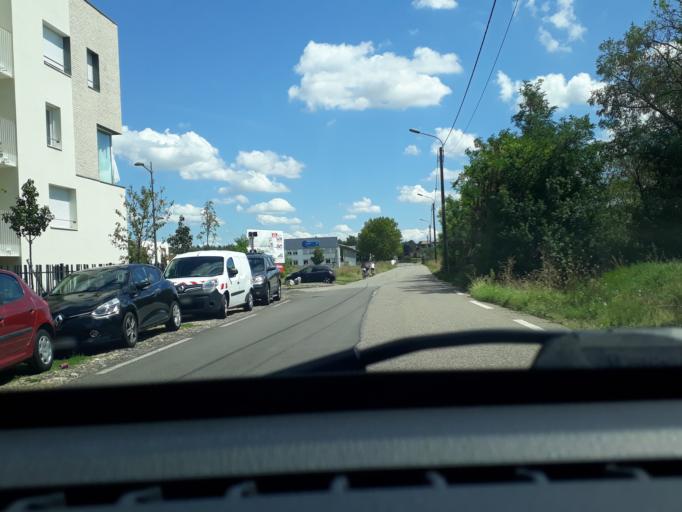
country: FR
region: Rhone-Alpes
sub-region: Departement du Rhone
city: Saint-Priest
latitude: 45.7056
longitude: 4.9216
